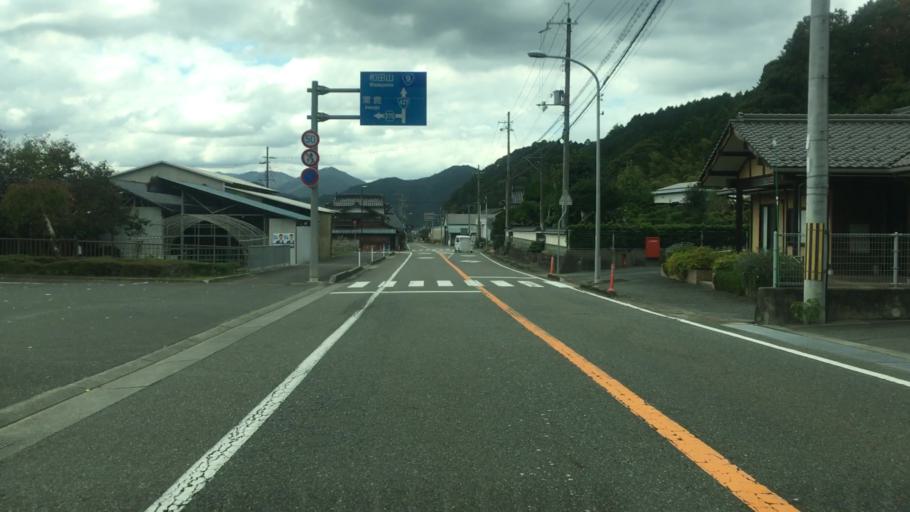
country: JP
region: Kyoto
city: Fukuchiyama
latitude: 35.3068
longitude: 134.9065
